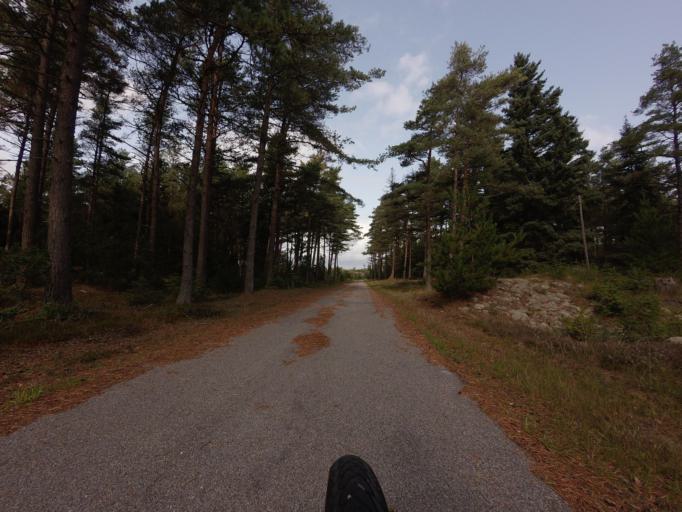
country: DK
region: North Denmark
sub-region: Frederikshavn Kommune
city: Strandby
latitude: 57.6356
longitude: 10.4337
